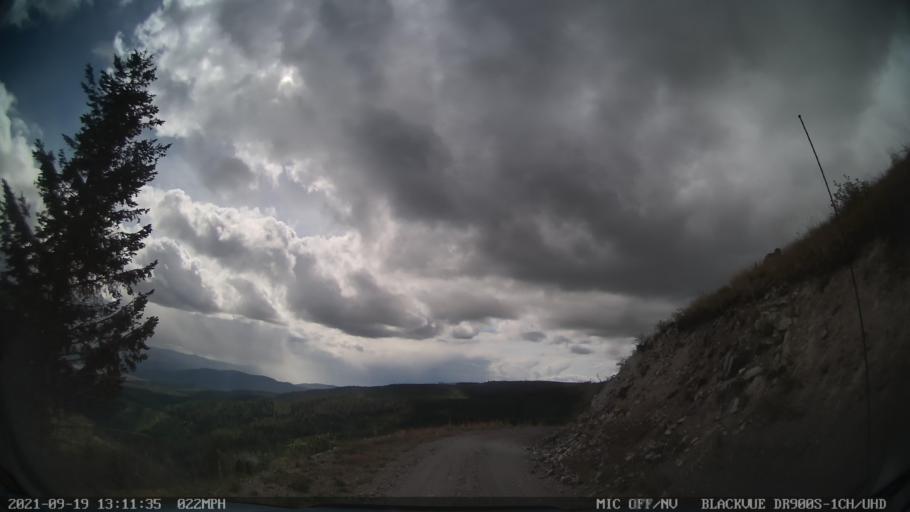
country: US
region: Montana
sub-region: Missoula County
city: Seeley Lake
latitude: 47.1738
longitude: -113.3494
